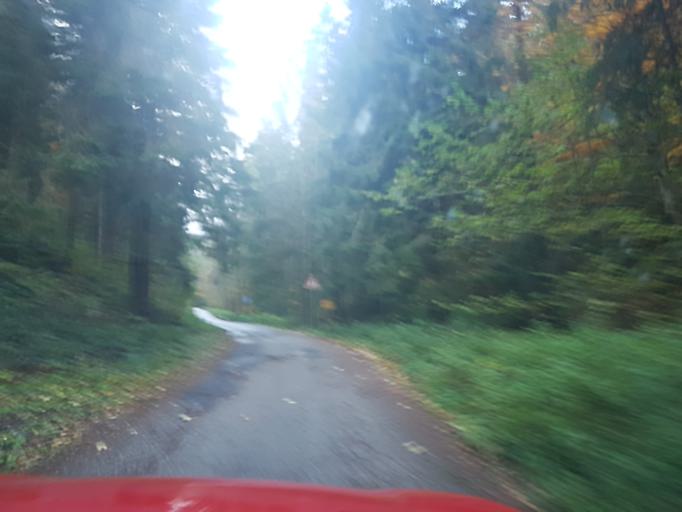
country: SK
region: Zilinsky
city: Ruzomberok
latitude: 48.9979
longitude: 19.2599
